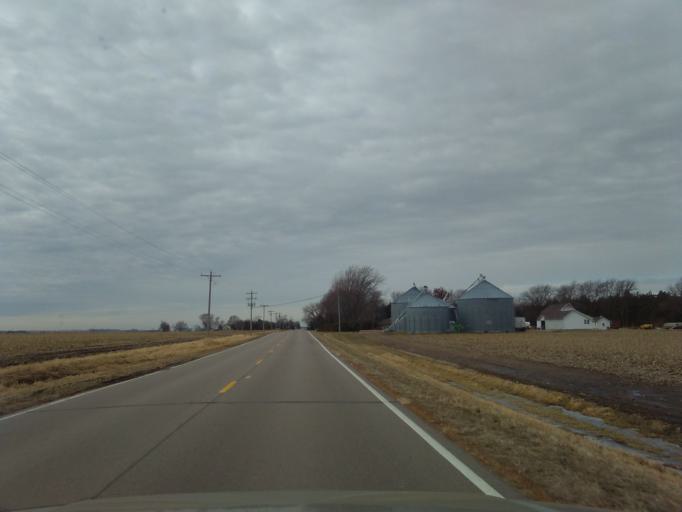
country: US
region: Nebraska
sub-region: Hall County
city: Grand Island
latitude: 40.7709
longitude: -98.4077
